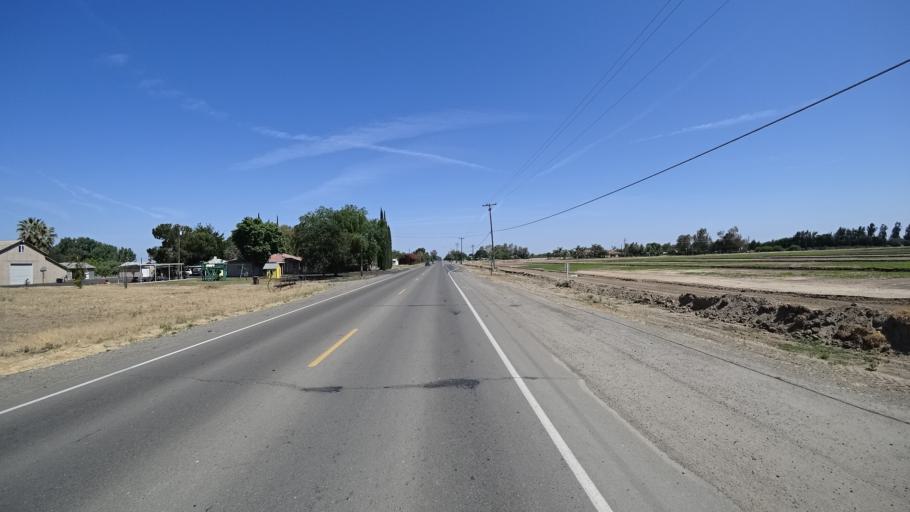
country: US
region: California
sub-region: Kings County
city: Lemoore
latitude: 36.2674
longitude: -119.7809
